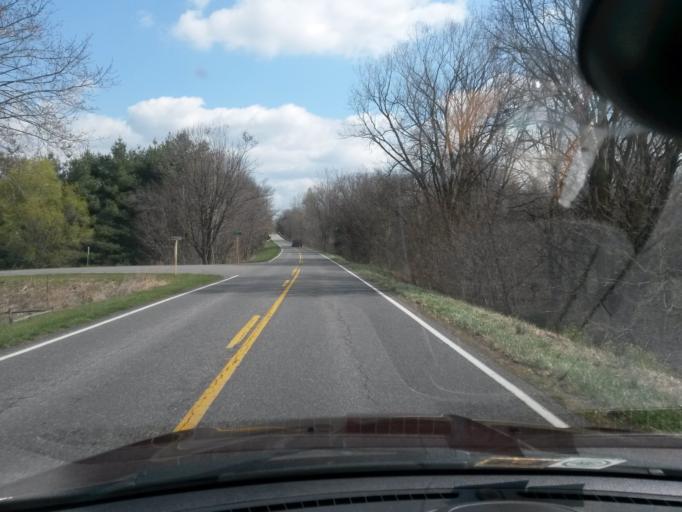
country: US
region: Virginia
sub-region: Augusta County
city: Weyers Cave
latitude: 38.3038
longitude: -78.8955
